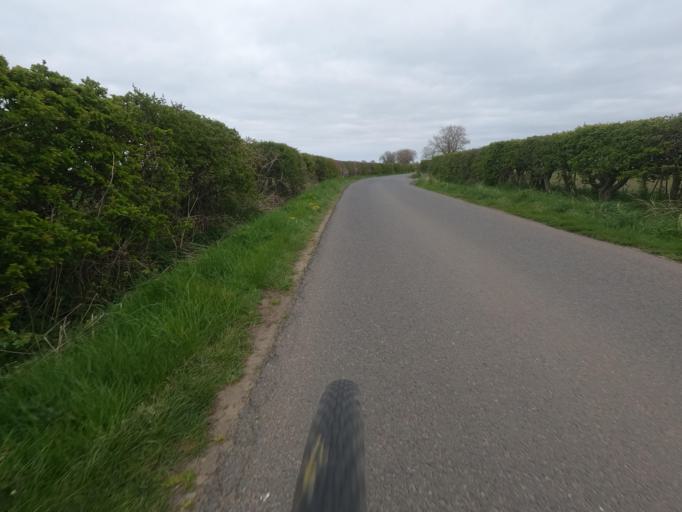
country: GB
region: England
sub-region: Northumberland
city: Darras Hall
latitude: 55.0773
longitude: -1.7924
